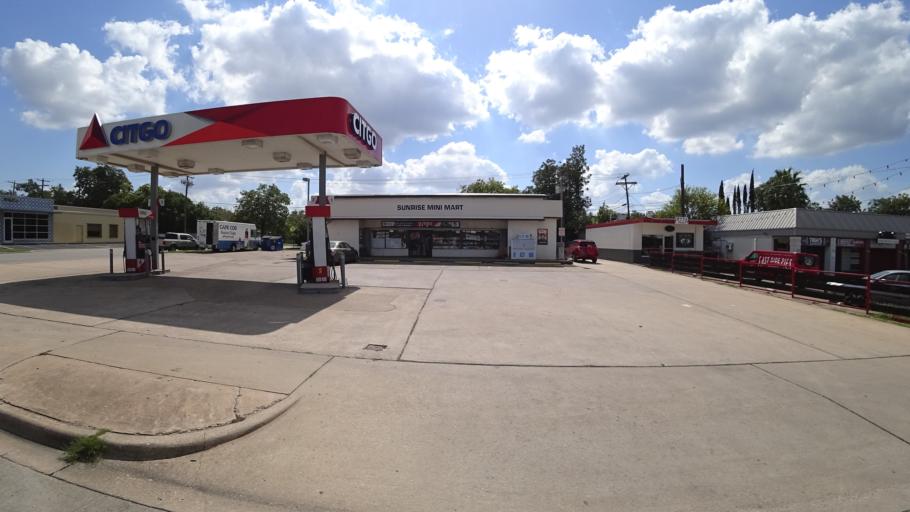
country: US
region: Texas
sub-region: Travis County
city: Austin
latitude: 30.3535
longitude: -97.7254
